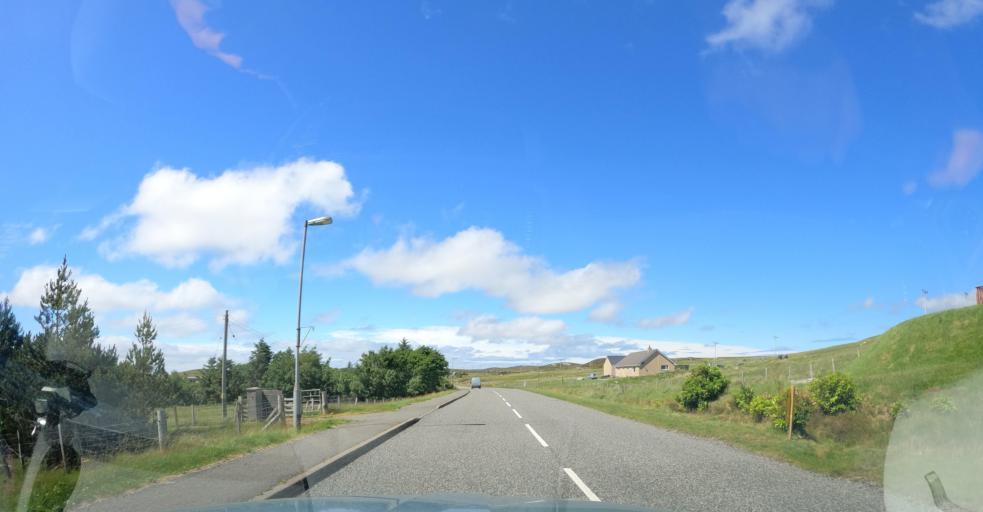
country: GB
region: Scotland
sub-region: Eilean Siar
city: Harris
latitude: 58.1899
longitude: -6.7065
